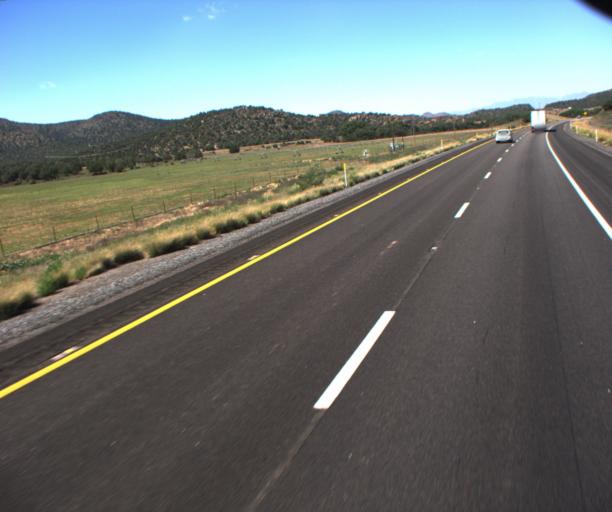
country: US
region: Arizona
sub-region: Mohave County
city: Peach Springs
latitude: 35.1853
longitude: -113.4543
